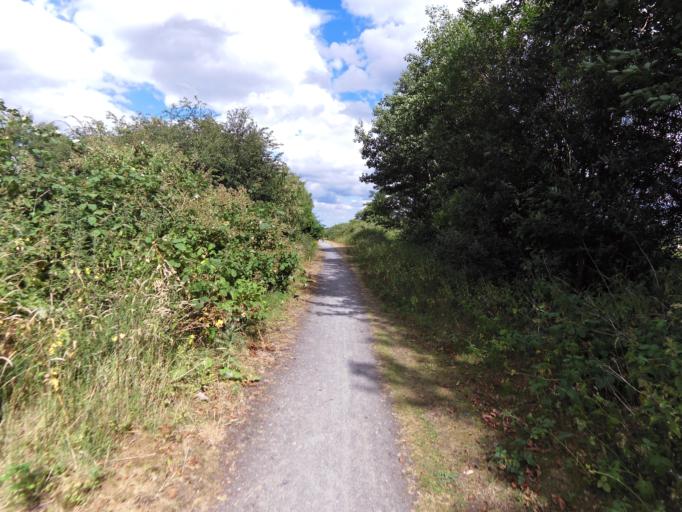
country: GB
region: England
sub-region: Norfolk
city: Ditchingham
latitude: 52.4646
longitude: 1.4492
